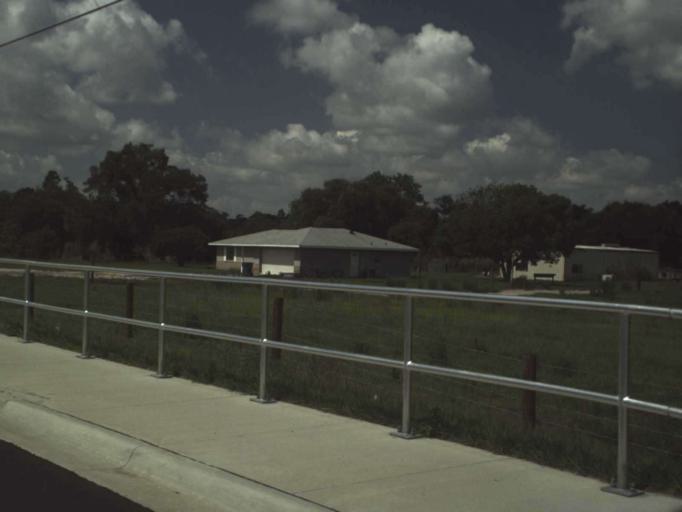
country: US
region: Florida
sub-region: Seminole County
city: Midway
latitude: 28.8619
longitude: -81.1623
